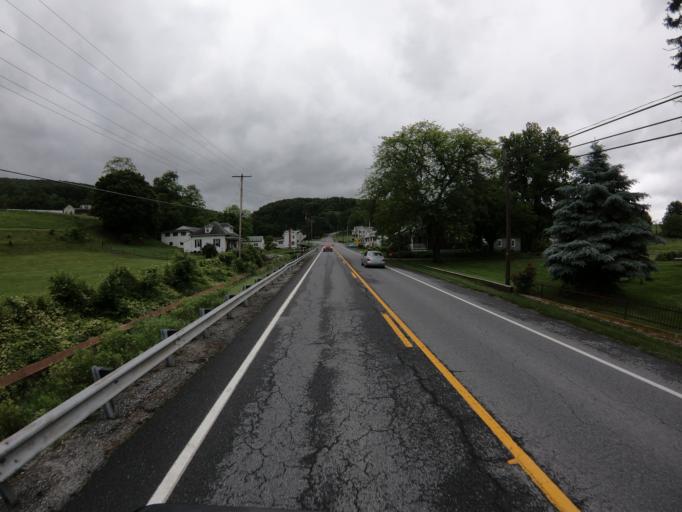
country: US
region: Maryland
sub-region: Washington County
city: Boonsboro
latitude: 39.4921
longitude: -77.6391
